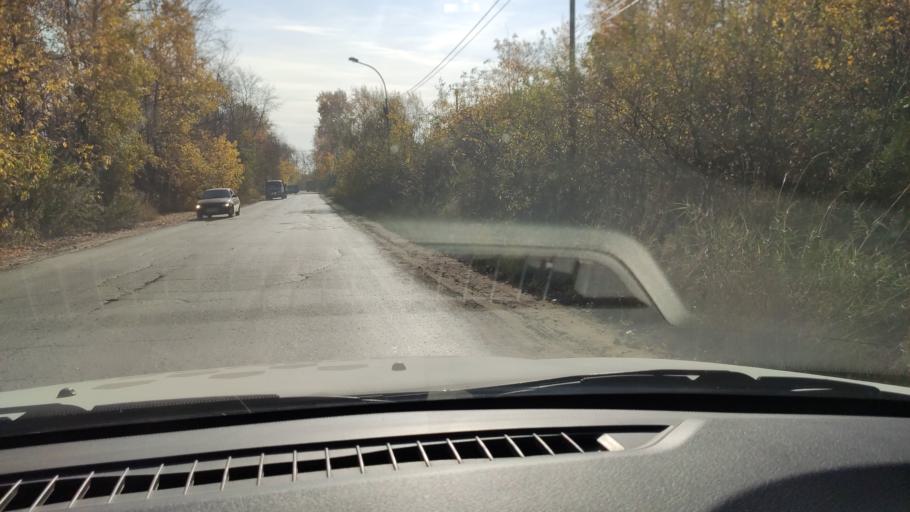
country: RU
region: Perm
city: Perm
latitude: 57.9578
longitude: 56.1955
